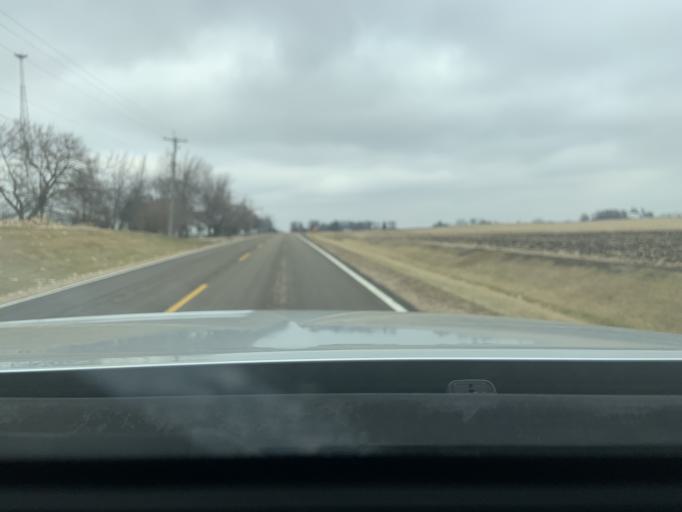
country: US
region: Illinois
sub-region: LaSalle County
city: Seneca
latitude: 41.3908
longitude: -88.6136
